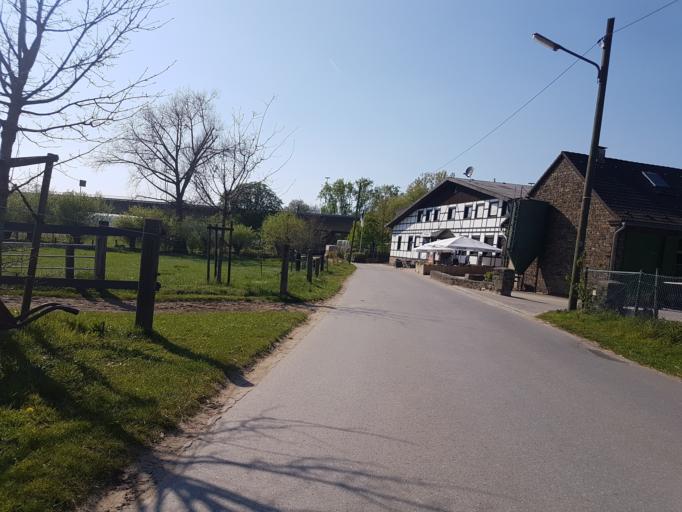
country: DE
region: North Rhine-Westphalia
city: Hattingen
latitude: 51.4213
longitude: 7.2127
